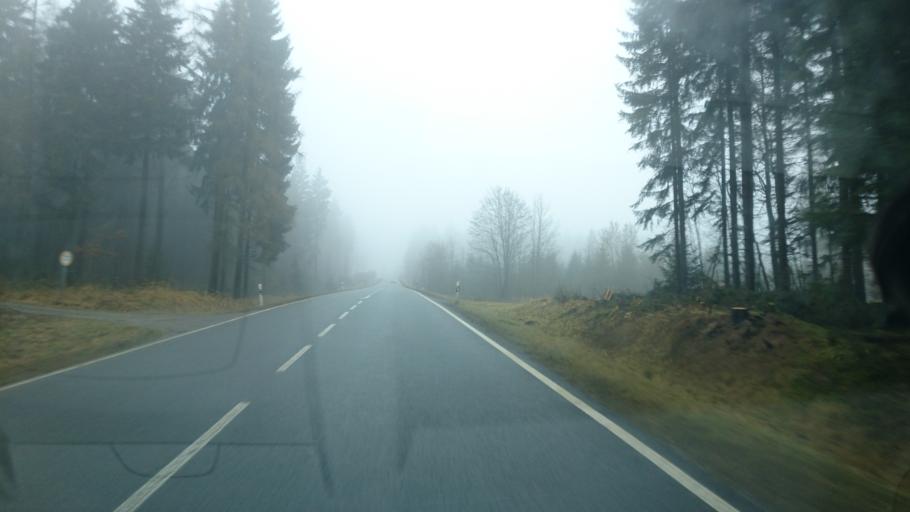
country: DE
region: Thuringia
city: Tanna
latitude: 50.4592
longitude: 11.8529
